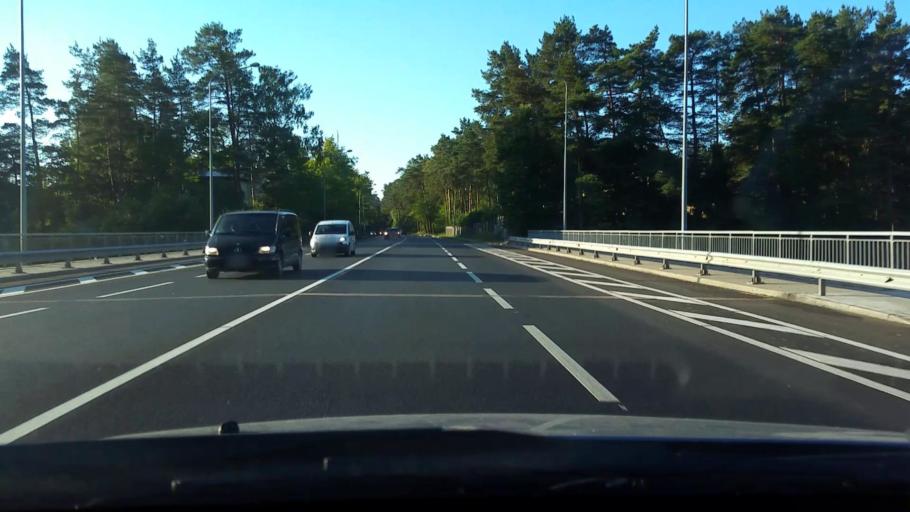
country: LV
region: Adazi
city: Adazi
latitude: 57.0412
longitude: 24.3154
